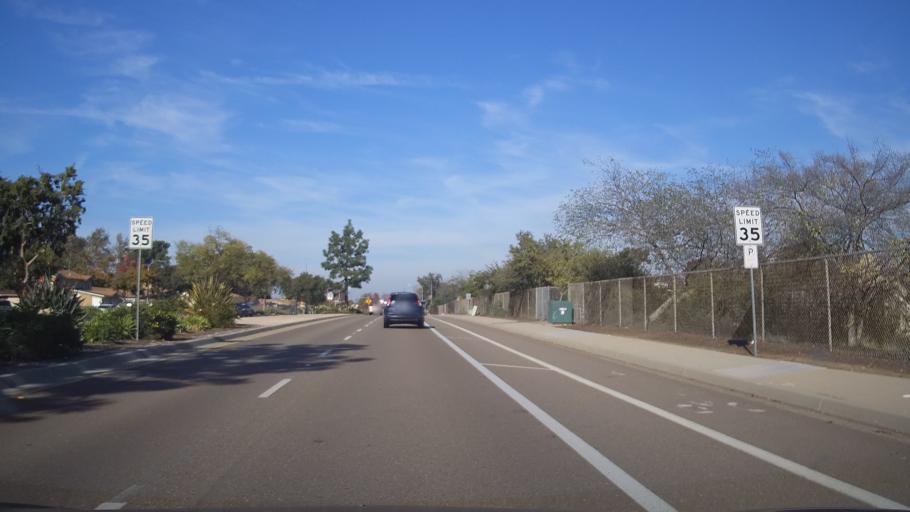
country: US
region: California
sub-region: San Diego County
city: La Mesa
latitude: 32.8205
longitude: -117.1039
